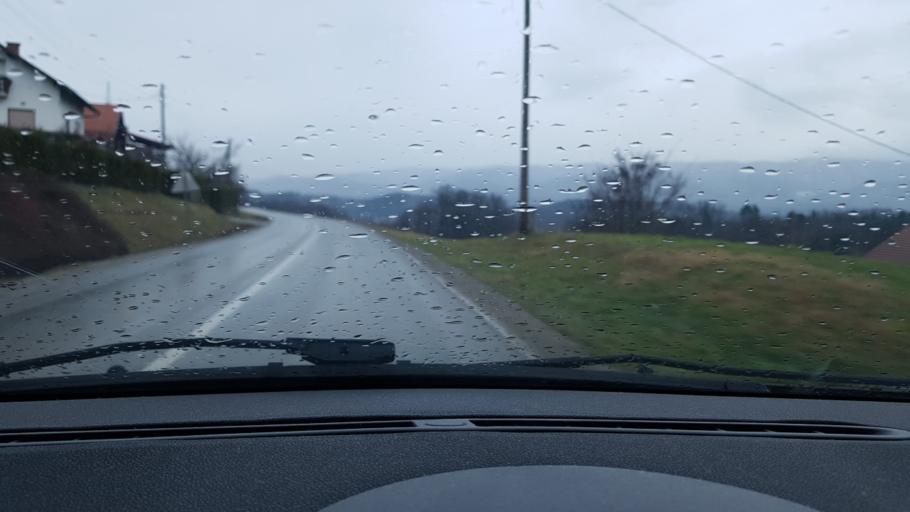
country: HR
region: Krapinsko-Zagorska
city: Oroslavje
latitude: 45.9781
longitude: 15.9059
